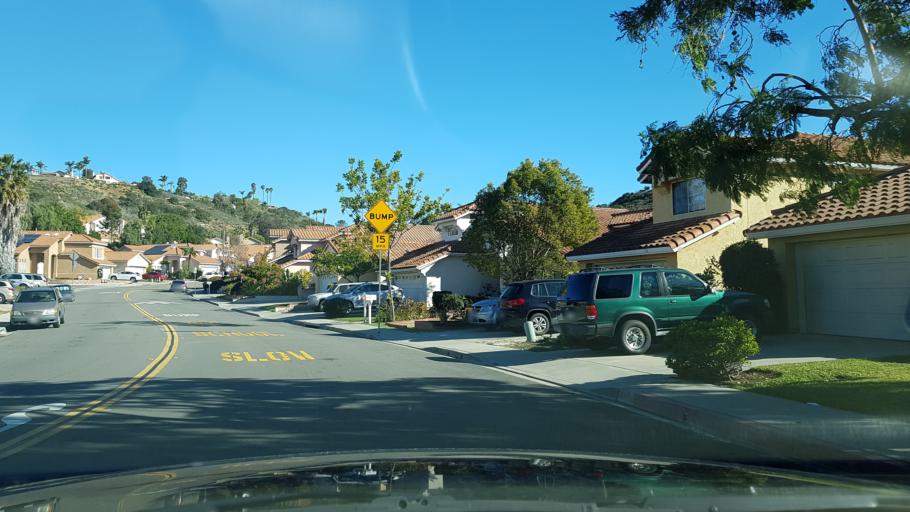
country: US
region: California
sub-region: San Diego County
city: Fairbanks Ranch
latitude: 32.9470
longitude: -117.1283
